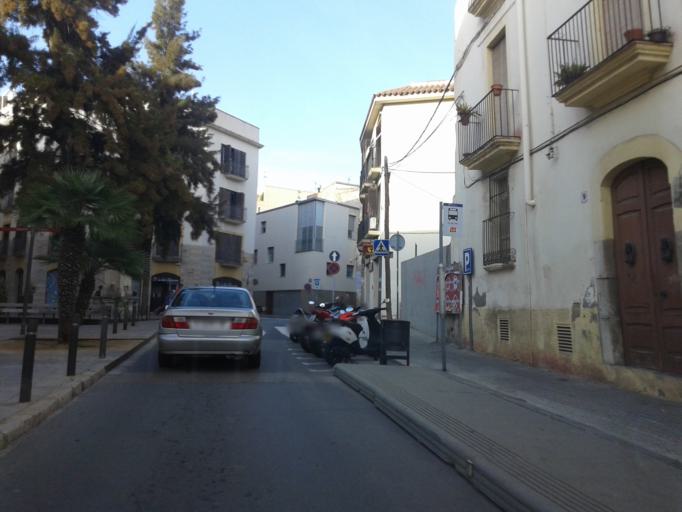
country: ES
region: Catalonia
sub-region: Provincia de Barcelona
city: Vilanova i la Geltru
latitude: 41.2268
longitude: 1.7271
